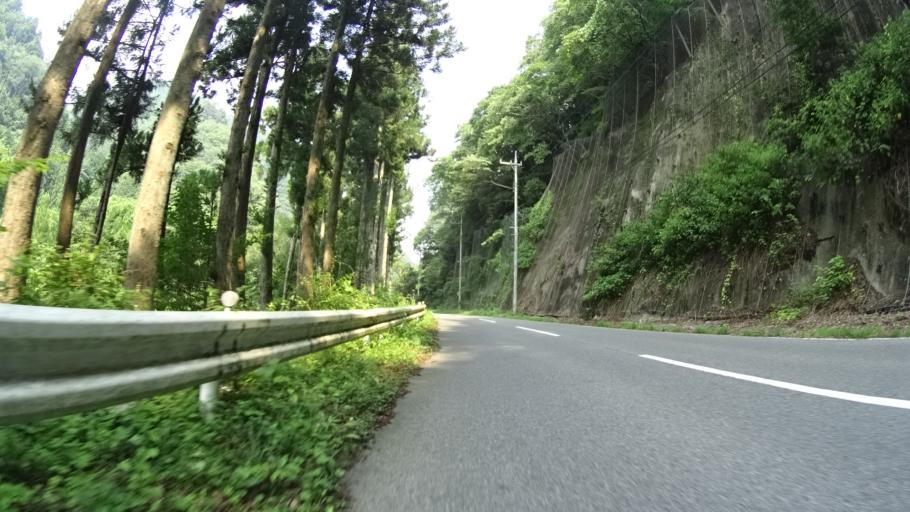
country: JP
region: Saitama
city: Chichibu
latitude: 36.0447
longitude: 138.8928
